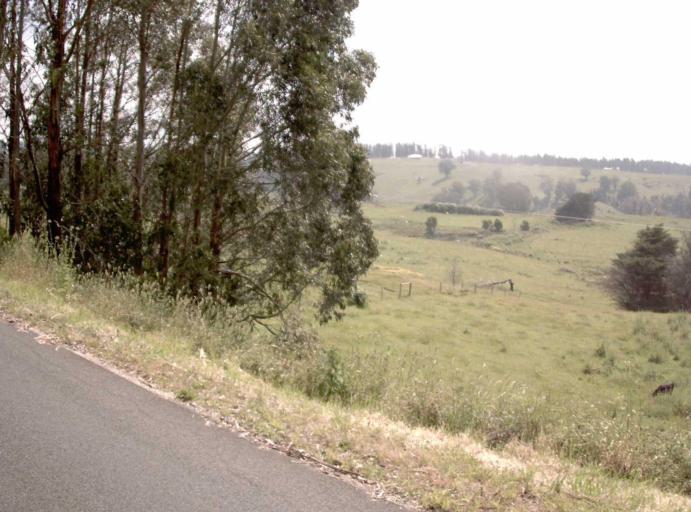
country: AU
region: Victoria
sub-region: Latrobe
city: Traralgon
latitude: -38.3384
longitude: 146.5733
